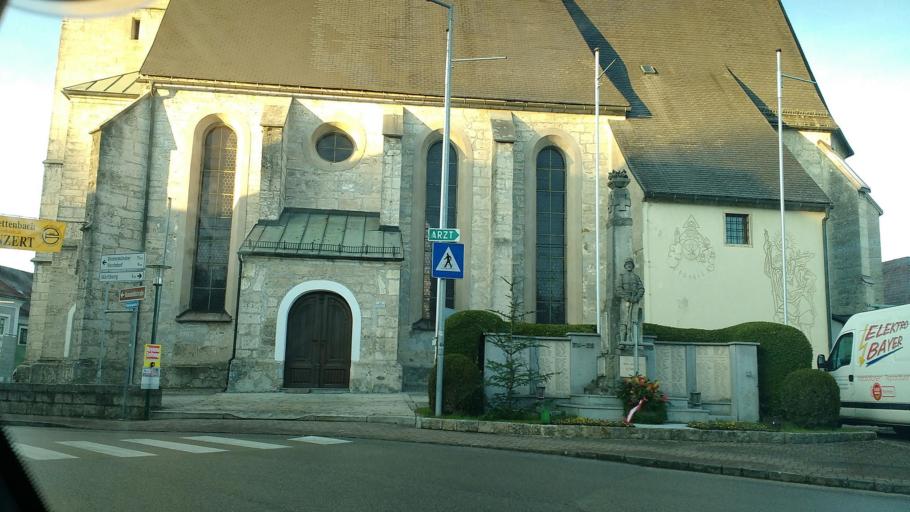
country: AT
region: Upper Austria
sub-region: Politischer Bezirk Gmunden
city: Scharnstein
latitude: 47.9607
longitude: 14.0169
